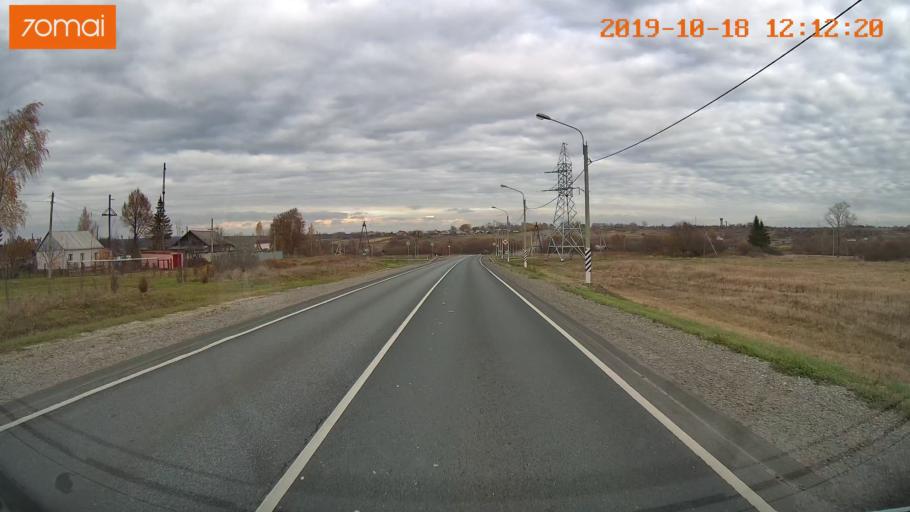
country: RU
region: Rjazan
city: Zakharovo
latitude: 54.4106
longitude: 39.3572
